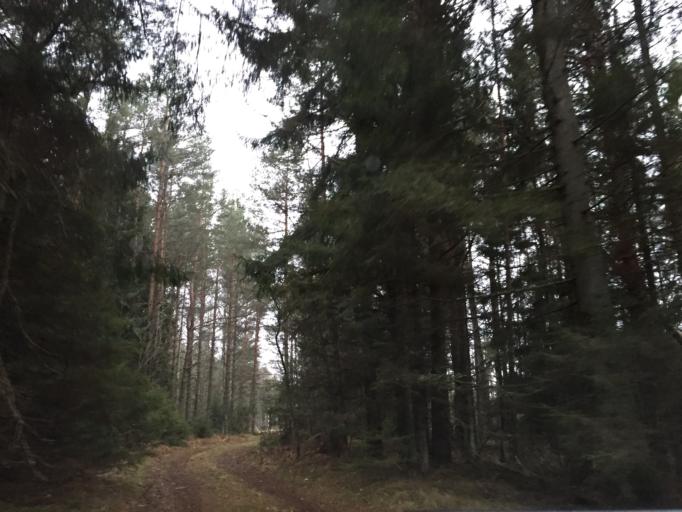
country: EE
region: Saare
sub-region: Kuressaare linn
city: Kuressaare
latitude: 58.4963
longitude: 22.3763
